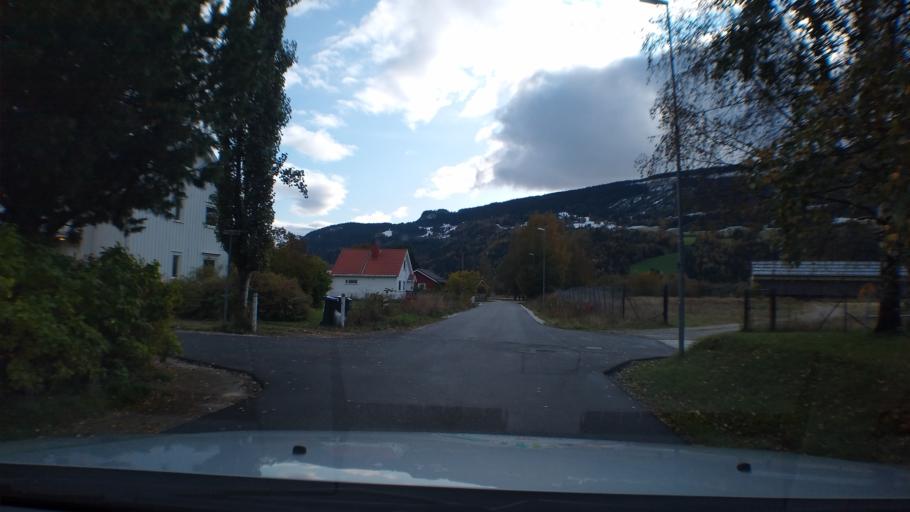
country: NO
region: Oppland
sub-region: Ringebu
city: Ringebu
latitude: 61.5262
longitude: 10.1470
